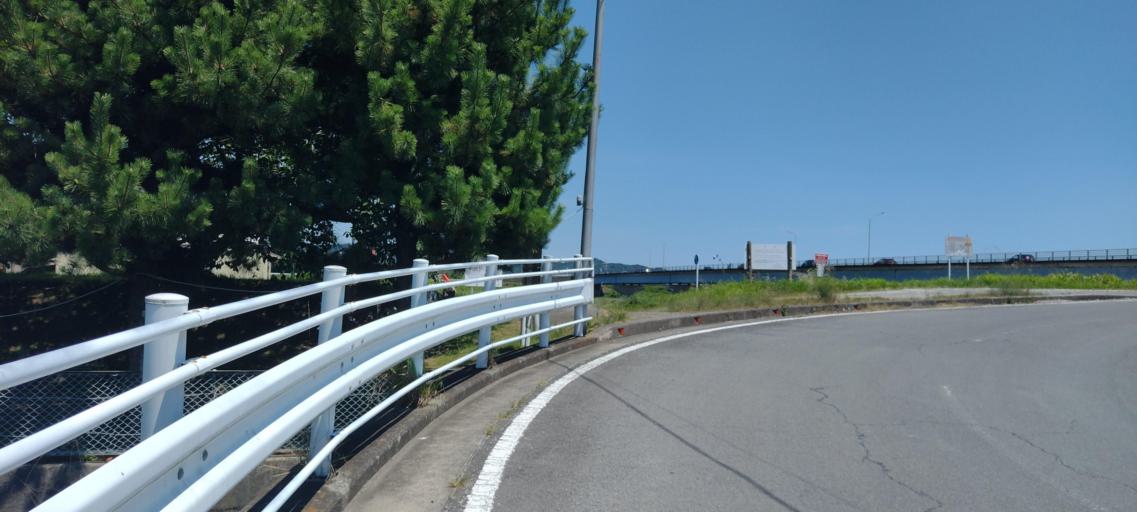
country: JP
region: Kanagawa
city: Odawara
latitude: 35.2967
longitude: 139.1543
